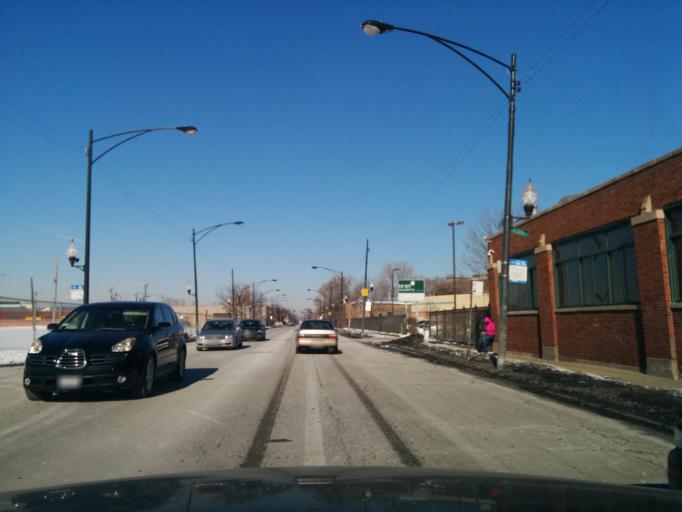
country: US
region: Illinois
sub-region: Cook County
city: Chicago
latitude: 41.8972
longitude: -87.7039
